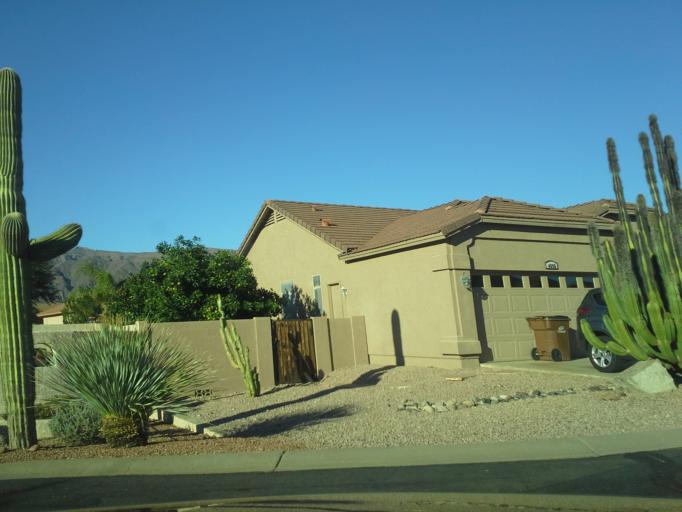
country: US
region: Arizona
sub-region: Pinal County
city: Apache Junction
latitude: 33.3723
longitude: -111.4366
